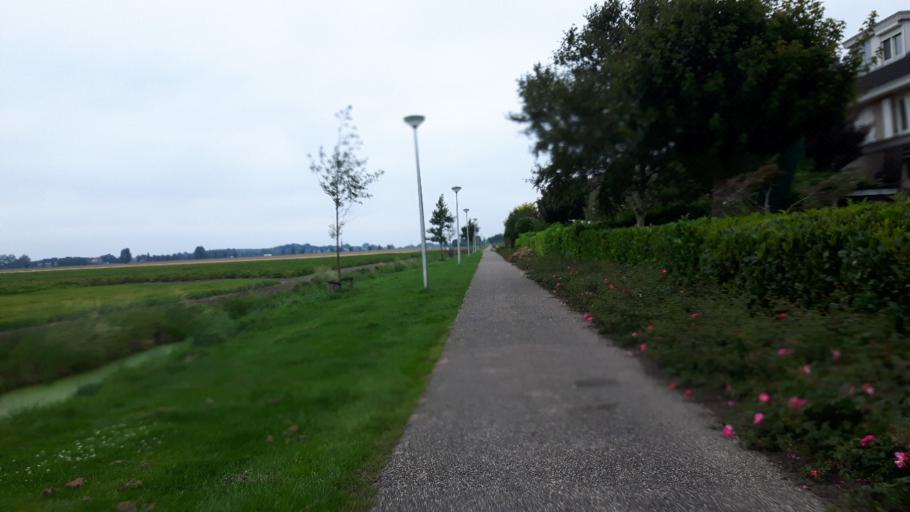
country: NL
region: South Holland
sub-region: Gemeente Nieuwkoop
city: Nieuwkoop
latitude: 52.1837
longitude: 4.7756
